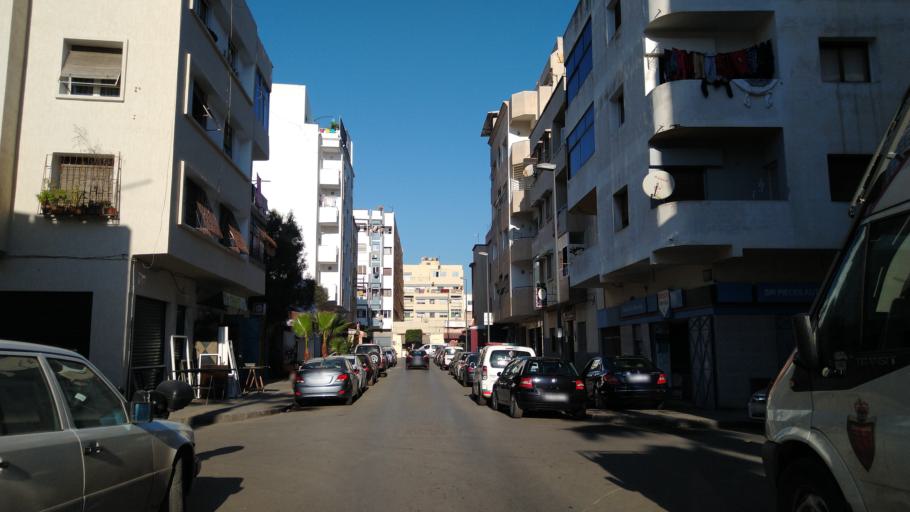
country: MA
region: Rabat-Sale-Zemmour-Zaer
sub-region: Rabat
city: Rabat
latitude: 34.0238
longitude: -6.8467
